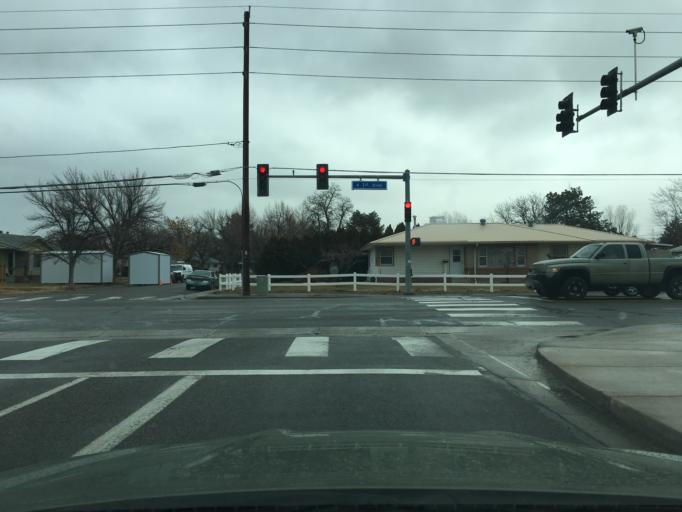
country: US
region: Colorado
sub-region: Mesa County
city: Grand Junction
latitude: 39.0809
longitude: -108.5711
